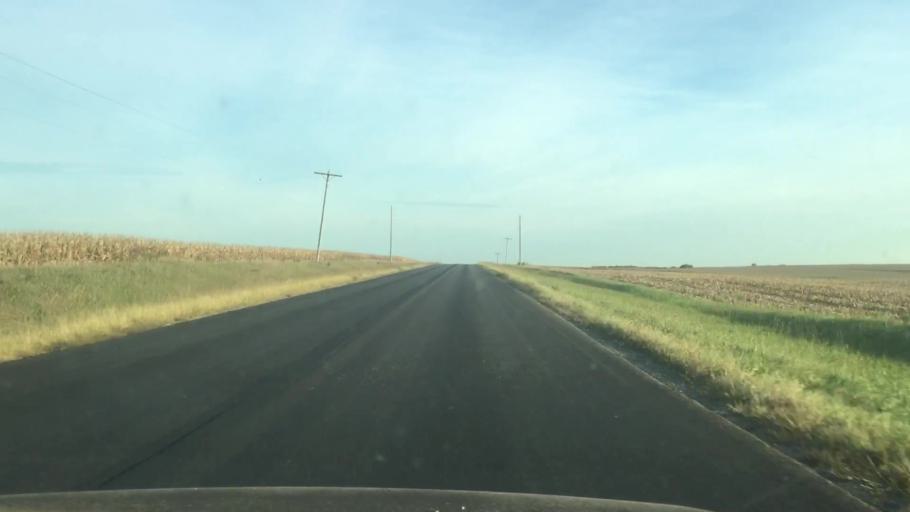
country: US
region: Kansas
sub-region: Marshall County
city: Marysville
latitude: 39.9053
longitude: -96.6010
